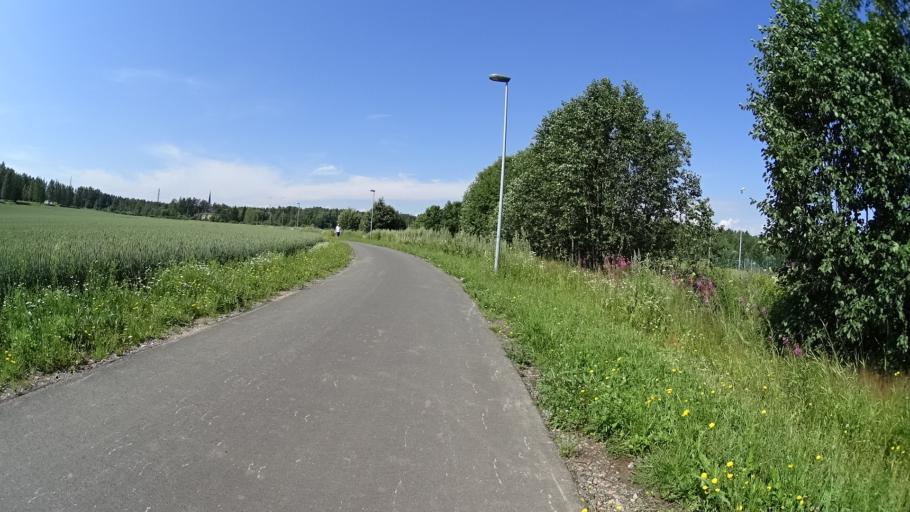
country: FI
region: Uusimaa
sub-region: Helsinki
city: Kilo
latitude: 60.2251
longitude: 24.7947
